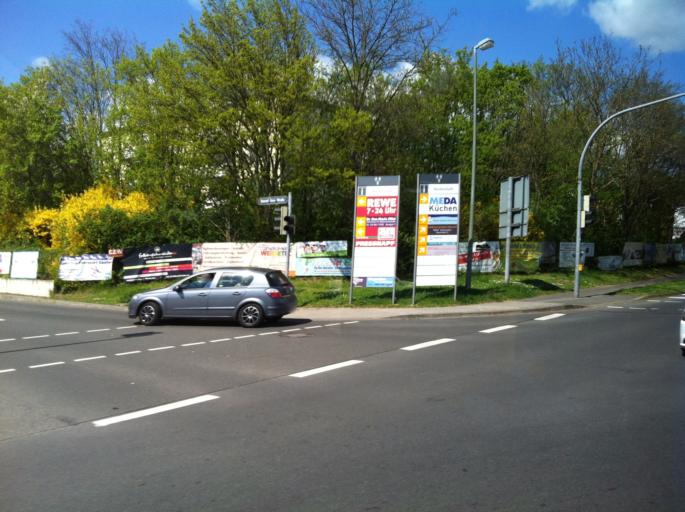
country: DE
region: Hesse
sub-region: Regierungsbezirk Darmstadt
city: Hochheim am Main
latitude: 50.0583
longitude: 8.3416
